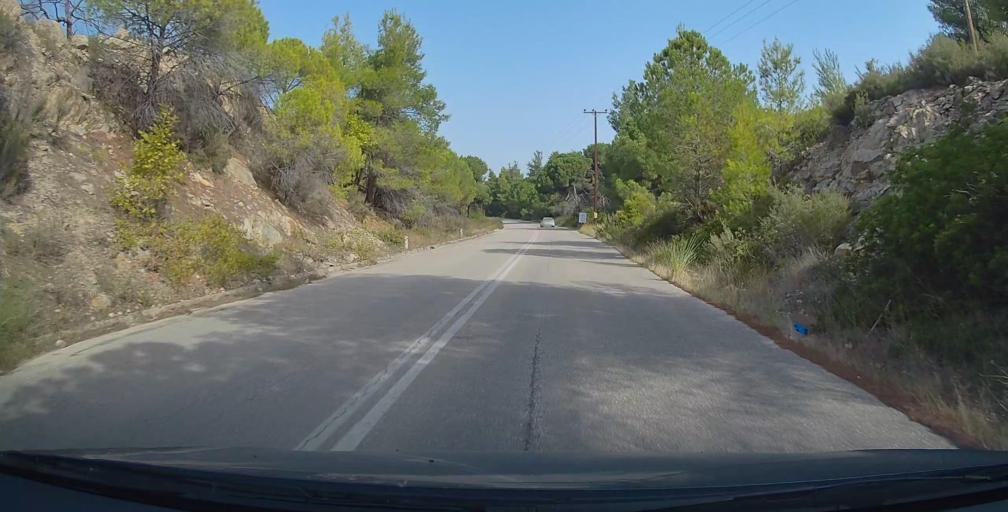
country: GR
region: Central Macedonia
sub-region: Nomos Chalkidikis
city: Sarti
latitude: 40.1189
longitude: 23.9707
